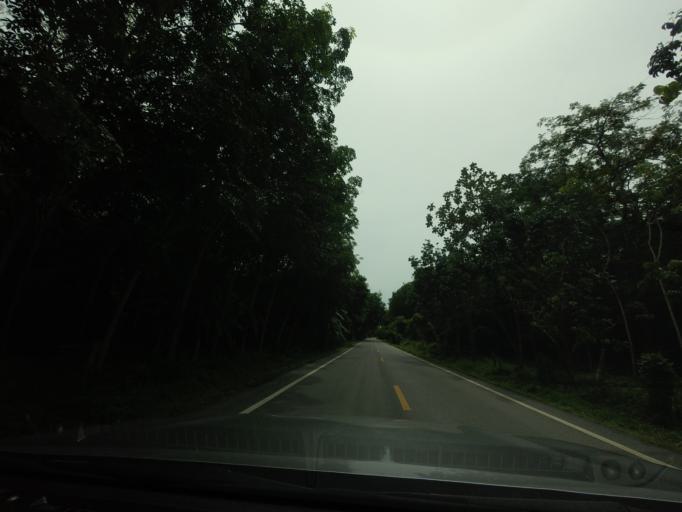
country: TH
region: Pattani
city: Kapho
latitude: 6.6026
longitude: 101.5329
